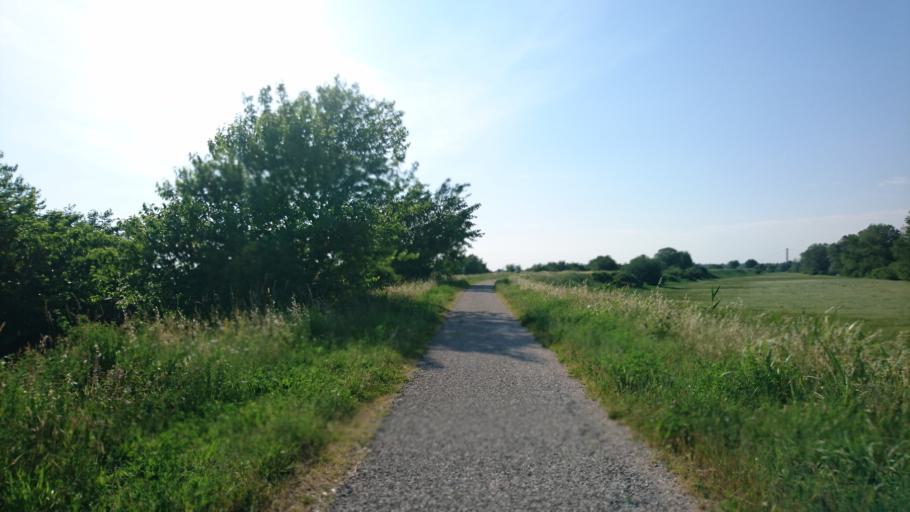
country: IT
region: Veneto
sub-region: Provincia di Verona
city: Boschi Sant'Anna
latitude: 45.1884
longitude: 11.3226
